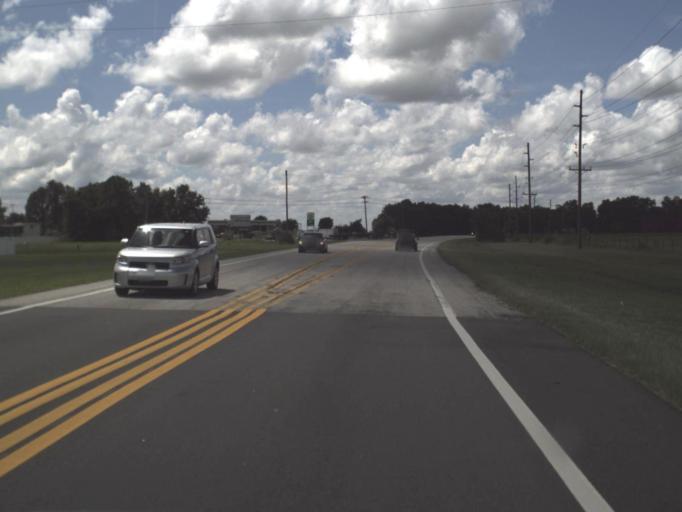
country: US
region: Florida
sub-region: Polk County
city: Polk City
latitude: 28.1642
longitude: -81.8572
